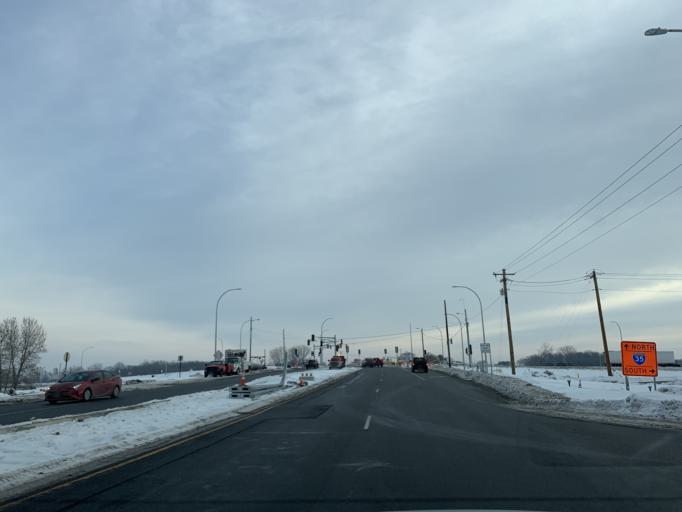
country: US
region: Minnesota
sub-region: Anoka County
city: Columbus
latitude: 45.2504
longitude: -93.0278
